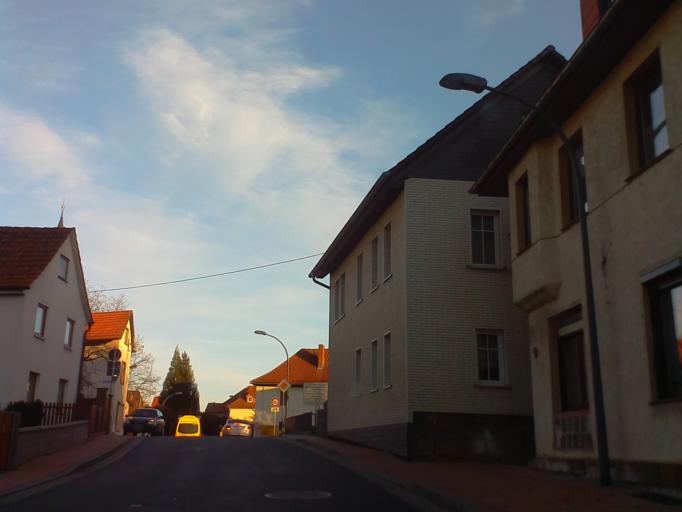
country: DE
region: Thuringia
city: Orlamunde
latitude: 50.7419
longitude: 11.4650
